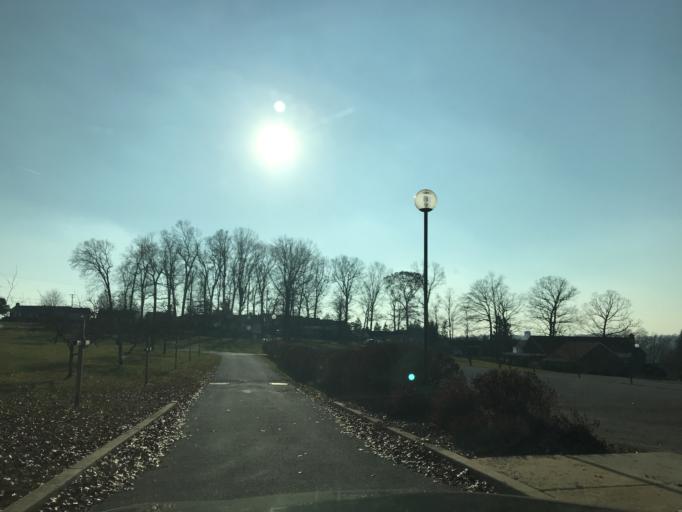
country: US
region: Pennsylvania
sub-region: York County
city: New Freedom
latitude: 39.7419
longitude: -76.6920
